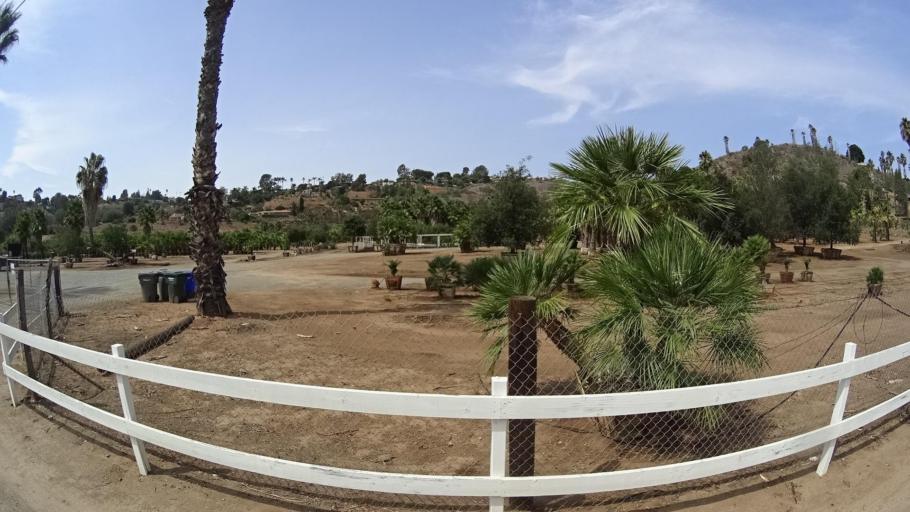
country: US
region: California
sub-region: San Diego County
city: Escondido
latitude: 33.0818
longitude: -117.0326
